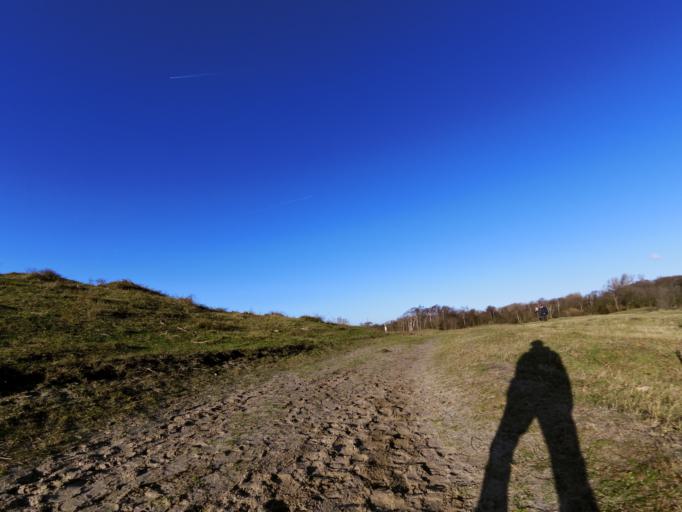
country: NL
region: South Holland
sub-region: Gemeente Goeree-Overflakkee
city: Goedereede
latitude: 51.8804
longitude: 4.0442
